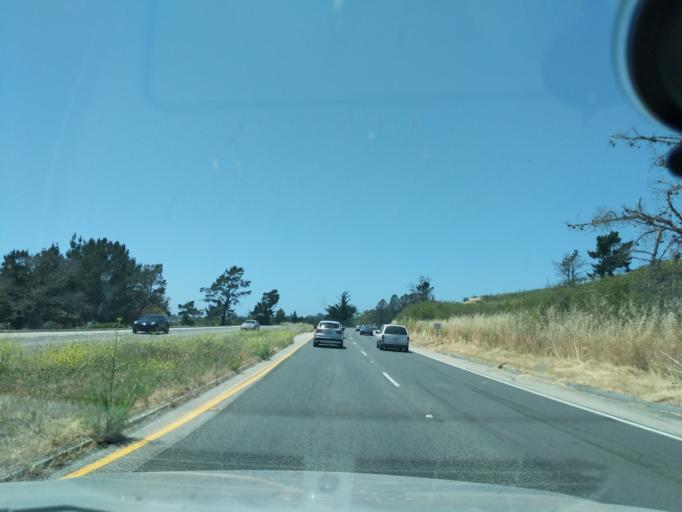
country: US
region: California
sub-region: Monterey County
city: Carmel-by-the-Sea
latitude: 36.5430
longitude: -121.8922
